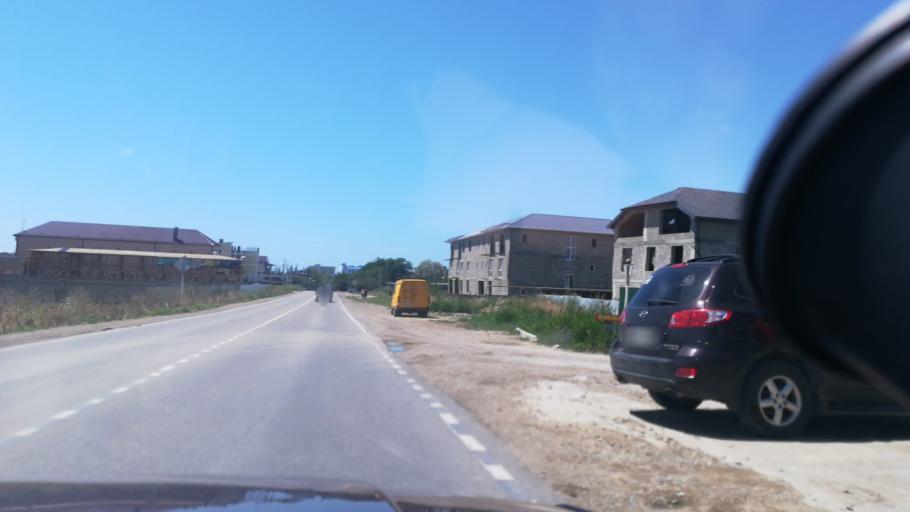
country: RU
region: Krasnodarskiy
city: Vityazevo
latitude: 44.9611
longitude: 37.3009
